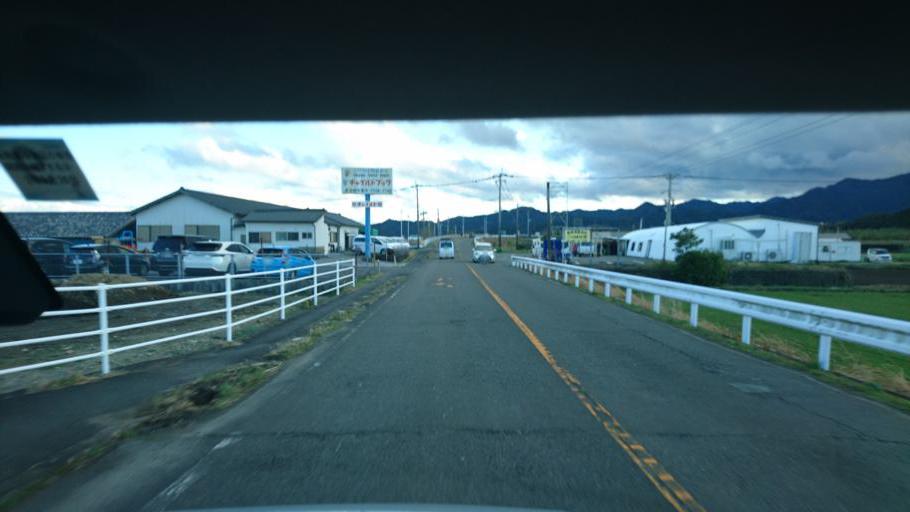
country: JP
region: Miyazaki
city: Miyazaki-shi
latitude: 31.8384
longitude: 131.4375
